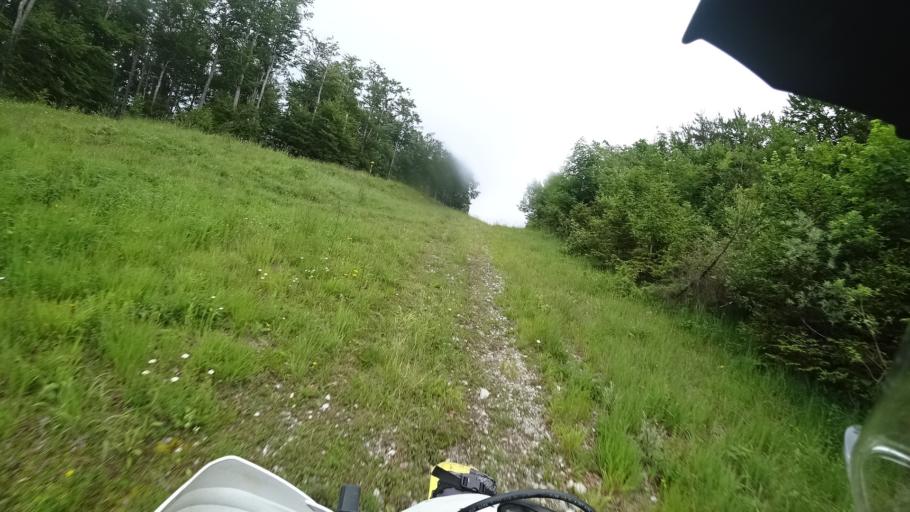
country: HR
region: Primorsko-Goranska
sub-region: Grad Delnice
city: Delnice
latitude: 45.3973
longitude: 14.8151
